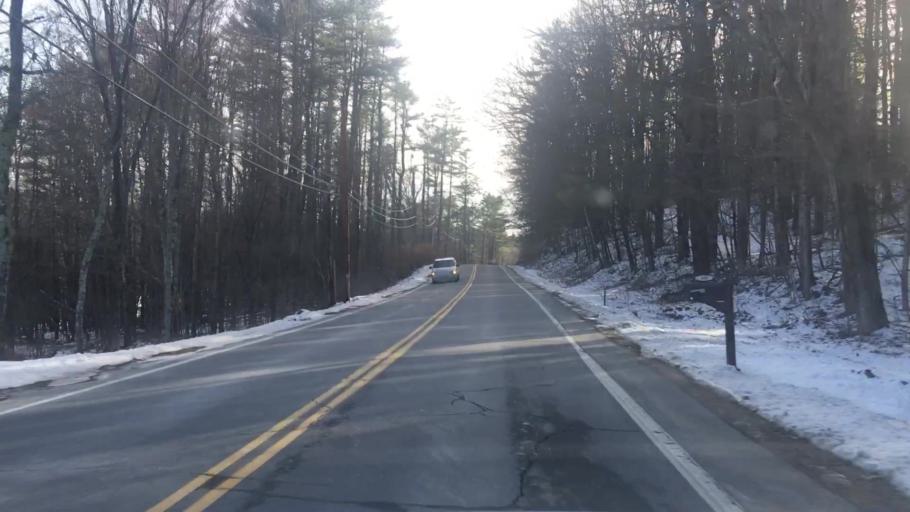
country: US
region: New Hampshire
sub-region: Merrimack County
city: Canterbury
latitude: 43.3053
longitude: -71.5670
